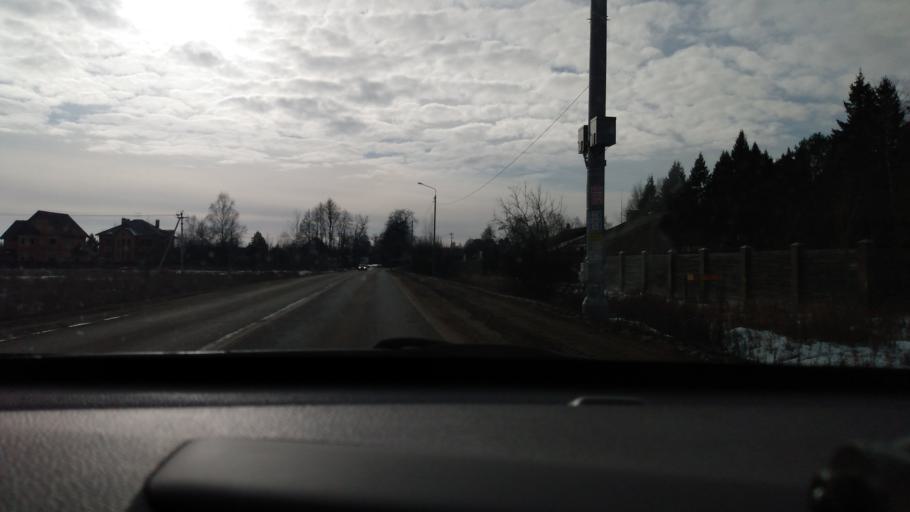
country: RU
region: Moskovskaya
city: Nakhabino
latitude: 55.8710
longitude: 37.1848
